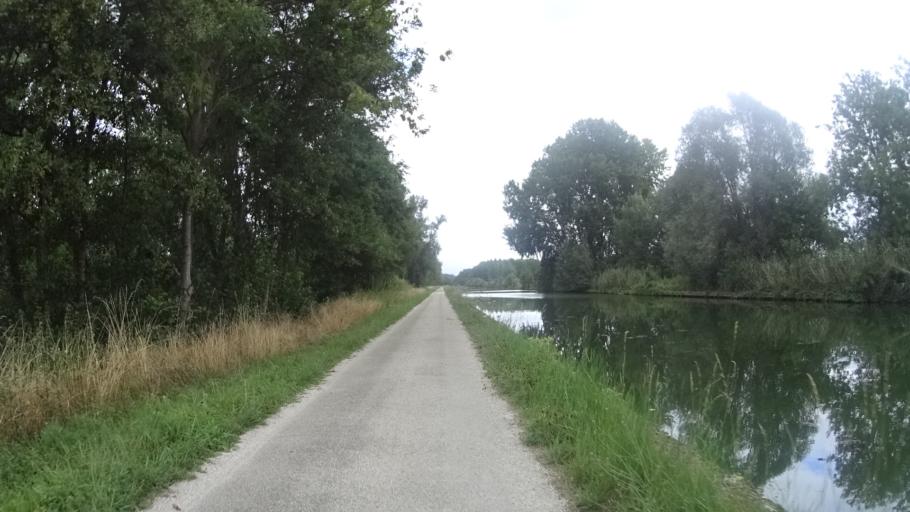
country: FR
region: Picardie
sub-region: Departement de l'Aisne
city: Ribemont
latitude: 49.7908
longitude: 3.4252
